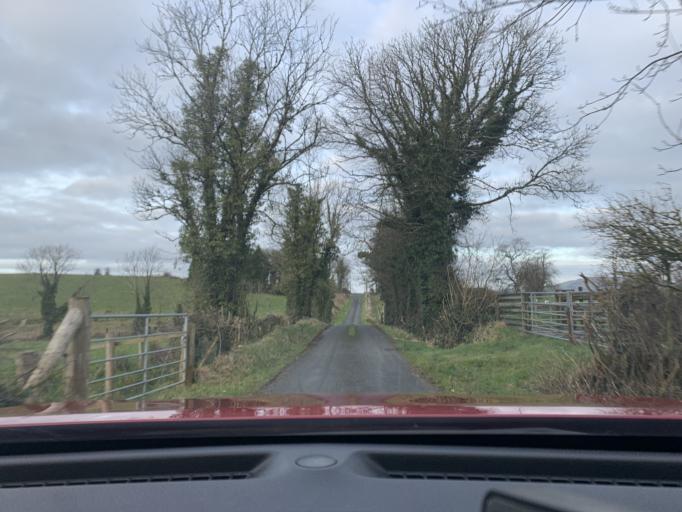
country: IE
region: Connaught
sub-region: Sligo
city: Ballymote
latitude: 54.0147
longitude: -8.5700
